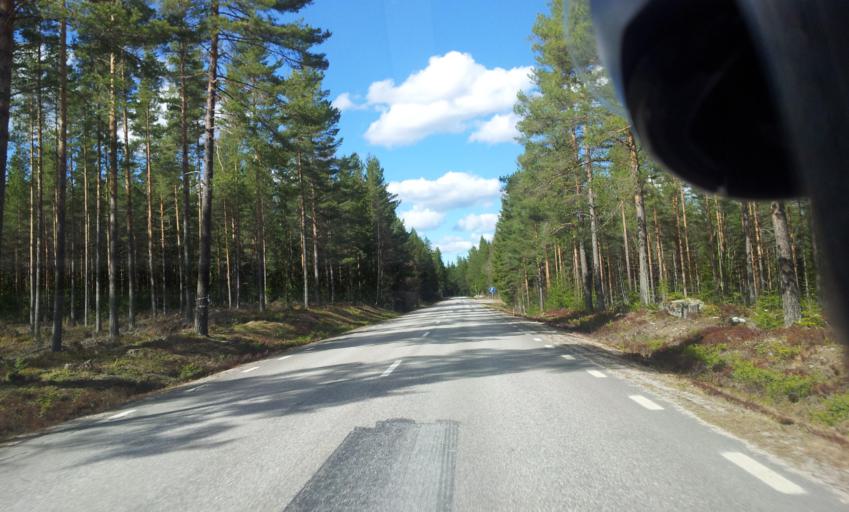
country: SE
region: Gaevleborg
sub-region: Ovanakers Kommun
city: Edsbyn
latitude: 61.3507
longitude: 15.8151
